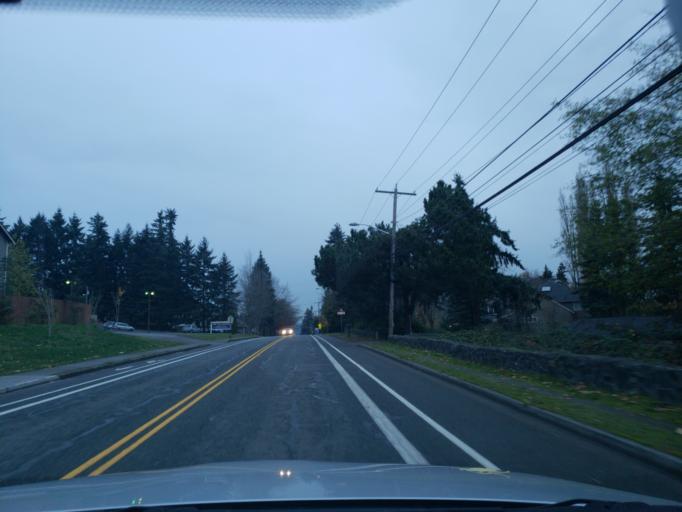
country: US
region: Washington
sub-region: King County
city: Inglewood-Finn Hill
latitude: 47.7425
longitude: -122.2264
